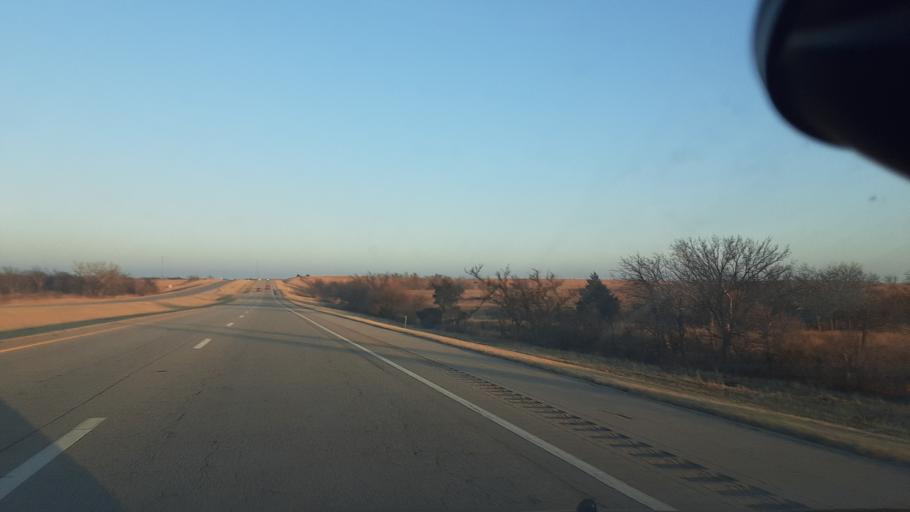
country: US
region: Oklahoma
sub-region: Noble County
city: Perry
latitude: 36.3980
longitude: -97.3667
